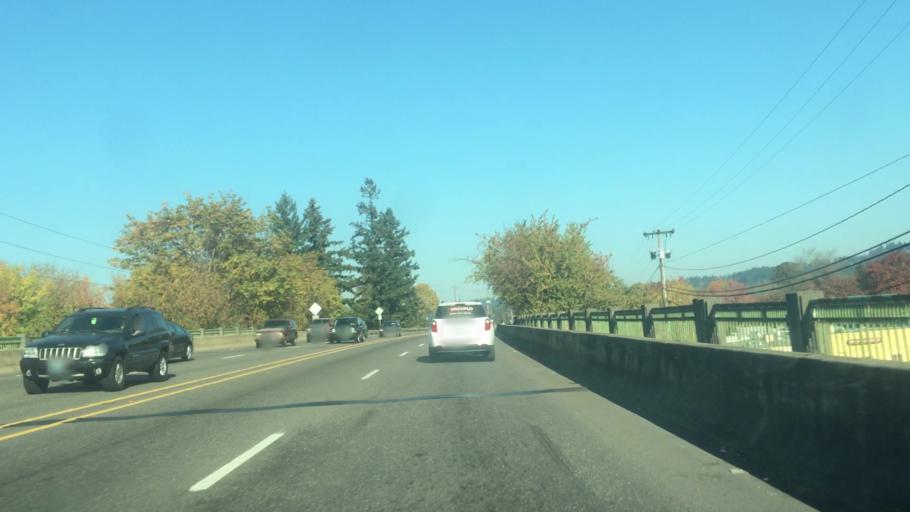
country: US
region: Oregon
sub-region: Washington County
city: Tigard
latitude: 45.4311
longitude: -122.7720
